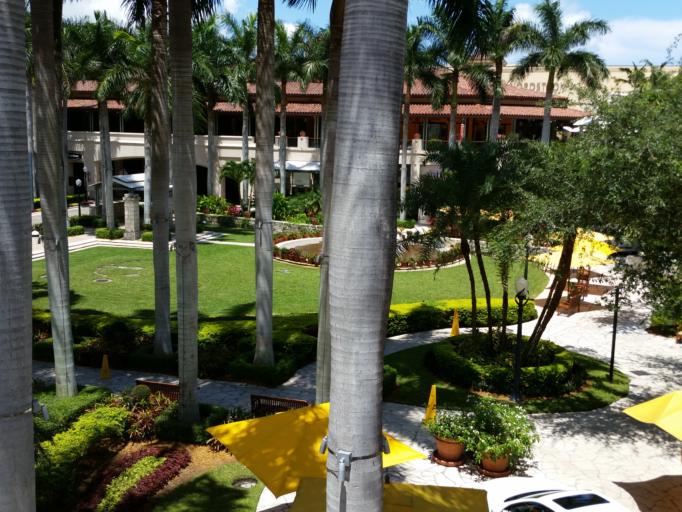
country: US
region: Florida
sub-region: Miami-Dade County
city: Coral Gables
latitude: 25.7318
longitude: -80.2606
